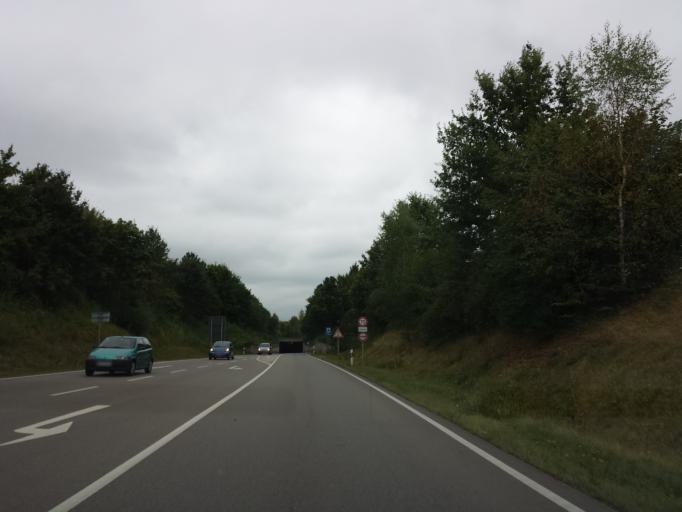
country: DE
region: Bavaria
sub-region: Swabia
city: Guenzburg
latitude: 48.4471
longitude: 10.2903
